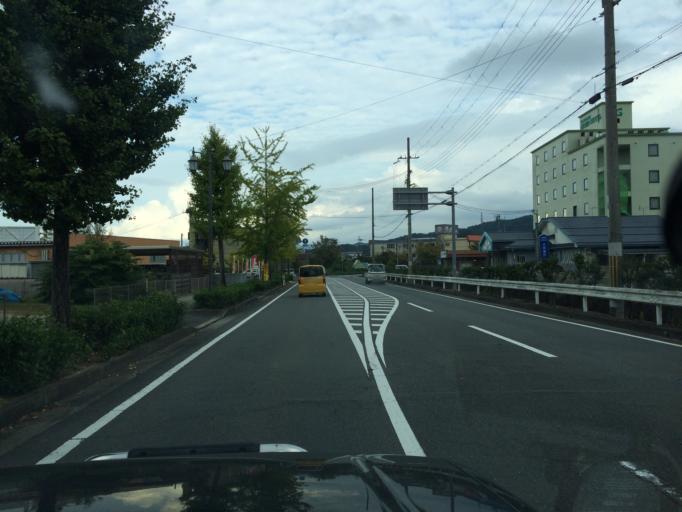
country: JP
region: Hyogo
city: Toyooka
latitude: 35.4702
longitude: 134.7742
